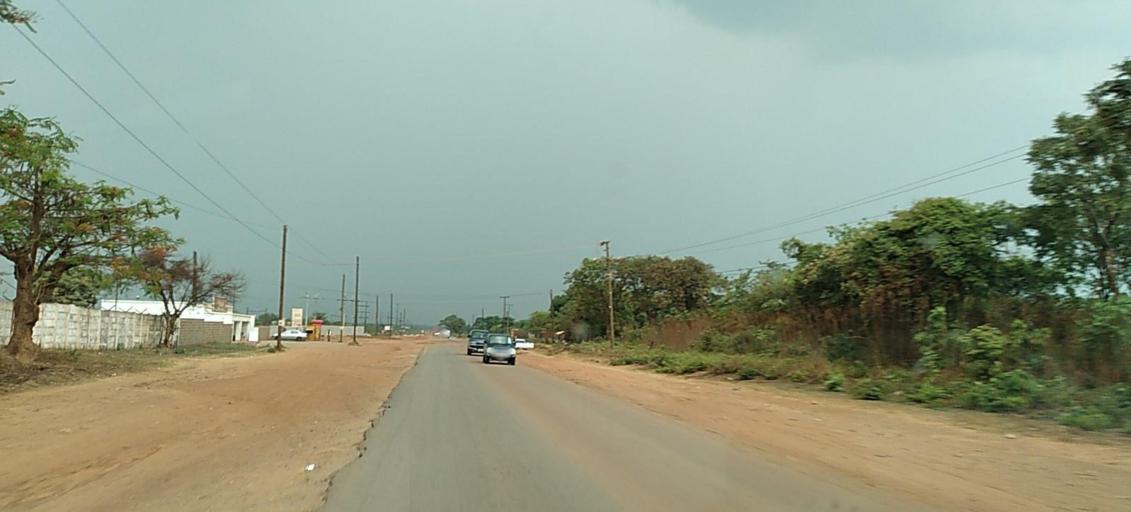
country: ZM
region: Copperbelt
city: Kalulushi
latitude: -12.8335
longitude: 28.1092
